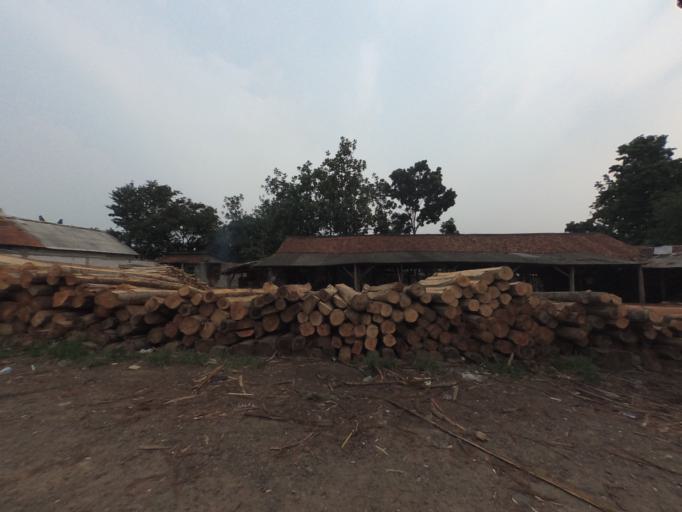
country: ID
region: West Java
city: Sidoger Lebak
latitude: -6.5659
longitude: 106.5995
